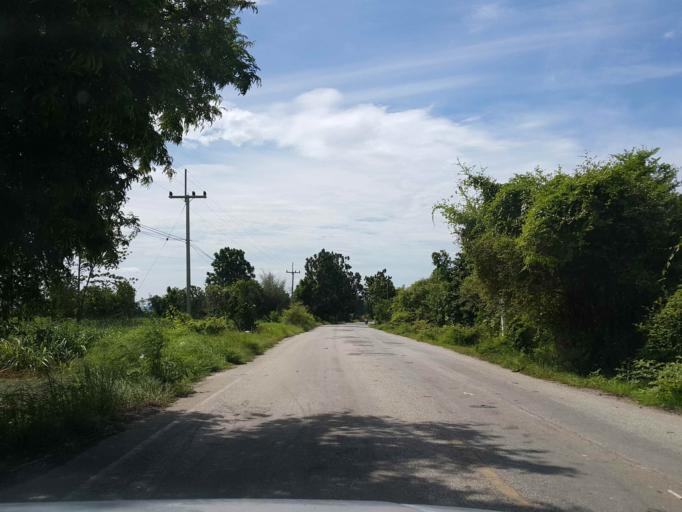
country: TH
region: Sukhothai
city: Ban Dan Lan Hoi
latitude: 17.1361
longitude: 99.5255
